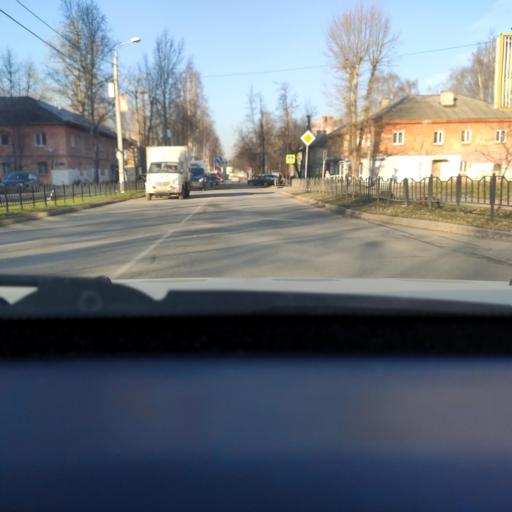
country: RU
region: Perm
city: Perm
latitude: 58.1078
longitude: 56.3797
